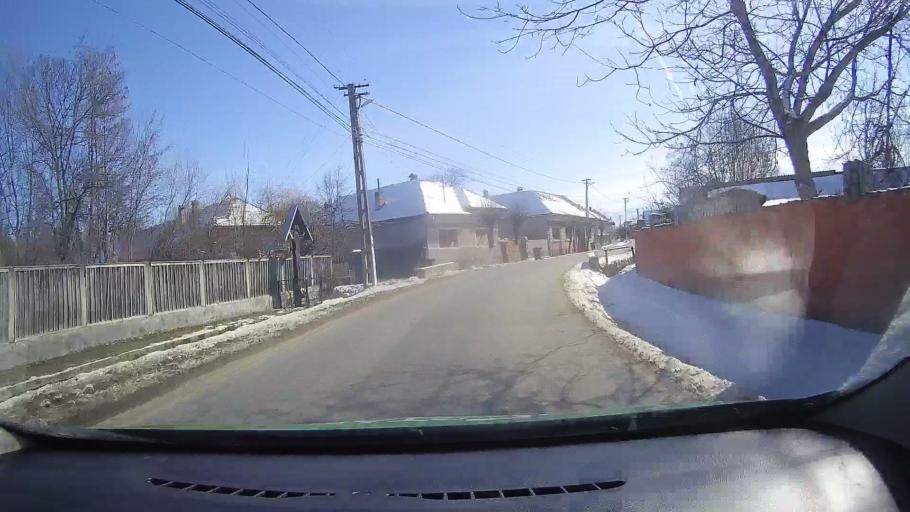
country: RO
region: Brasov
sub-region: Comuna Sambata de Sus
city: Sambata de Sus
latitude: 45.7613
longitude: 24.8221
